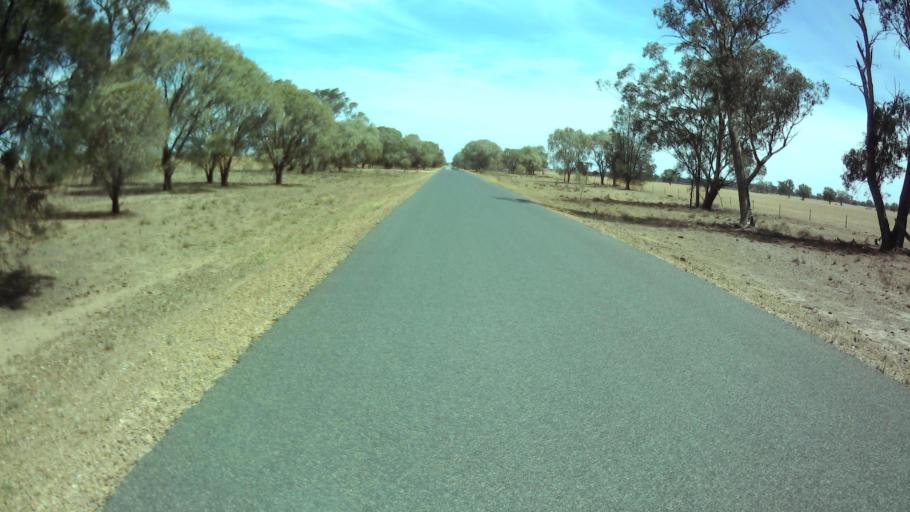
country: AU
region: New South Wales
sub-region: Weddin
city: Grenfell
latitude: -33.8697
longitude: 147.7450
